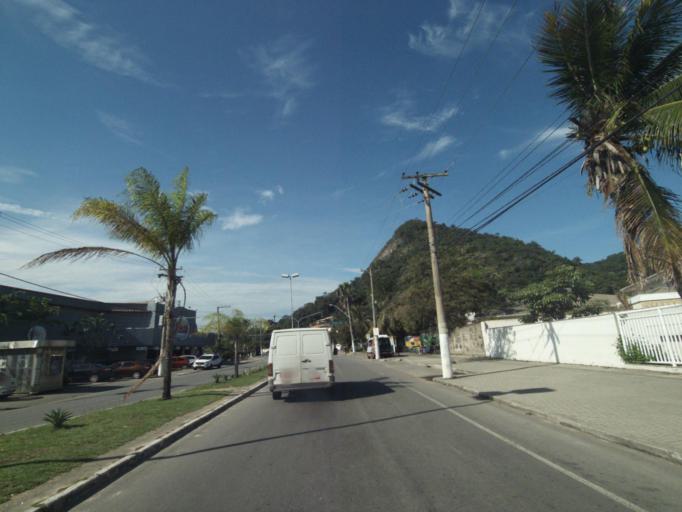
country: BR
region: Rio de Janeiro
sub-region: Niteroi
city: Niteroi
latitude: -22.9635
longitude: -43.0313
